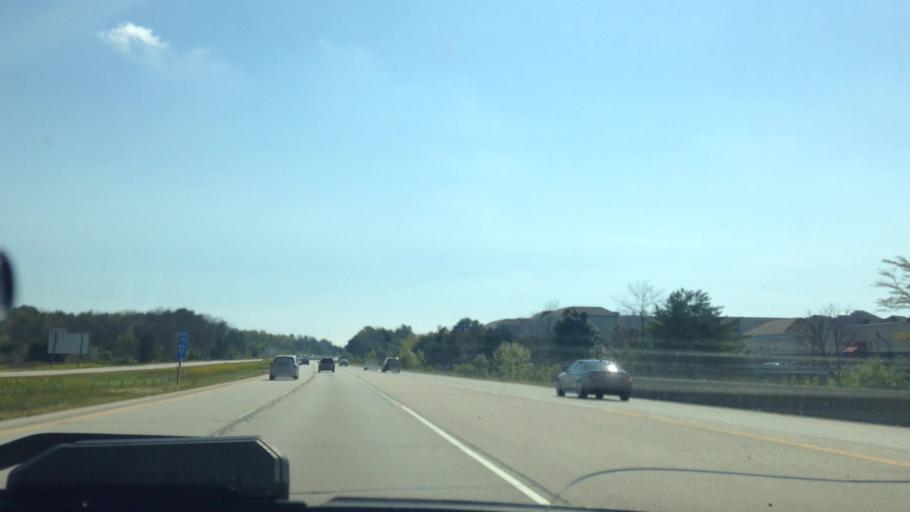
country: US
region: Wisconsin
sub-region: Milwaukee County
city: Bayside
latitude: 43.2187
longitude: -87.9218
